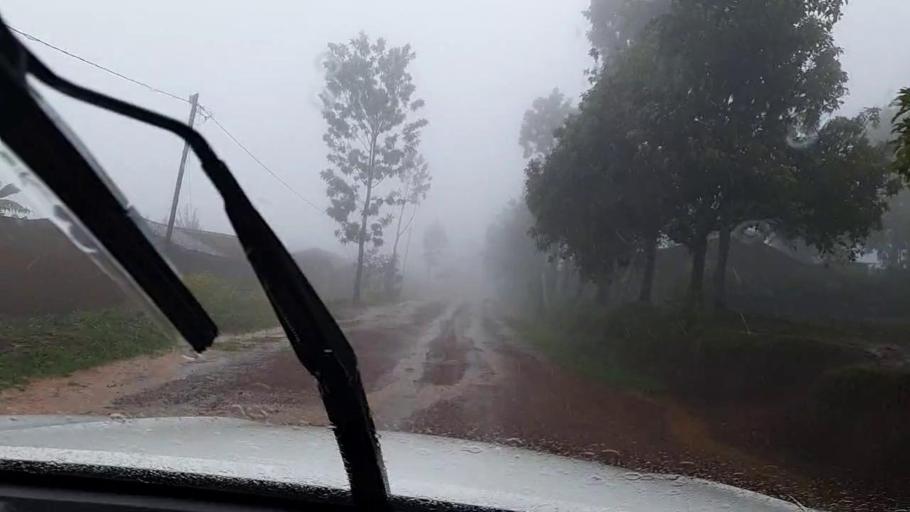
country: RW
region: Northern Province
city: Byumba
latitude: -1.7326
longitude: 30.0148
